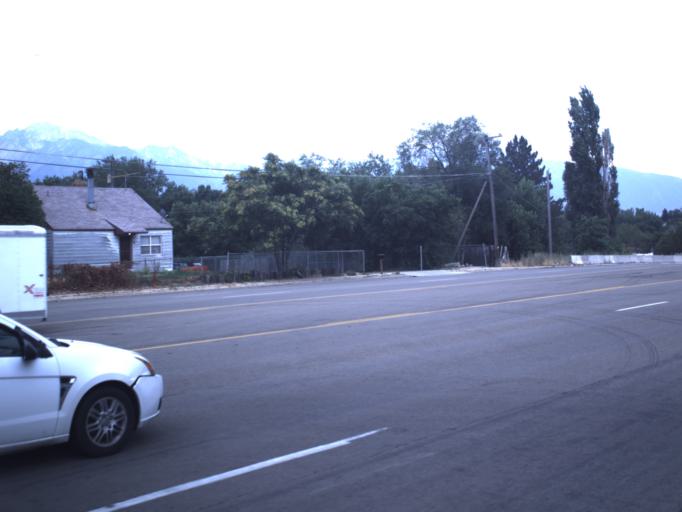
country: US
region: Utah
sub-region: Salt Lake County
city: Millcreek
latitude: 40.6715
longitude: -111.8717
